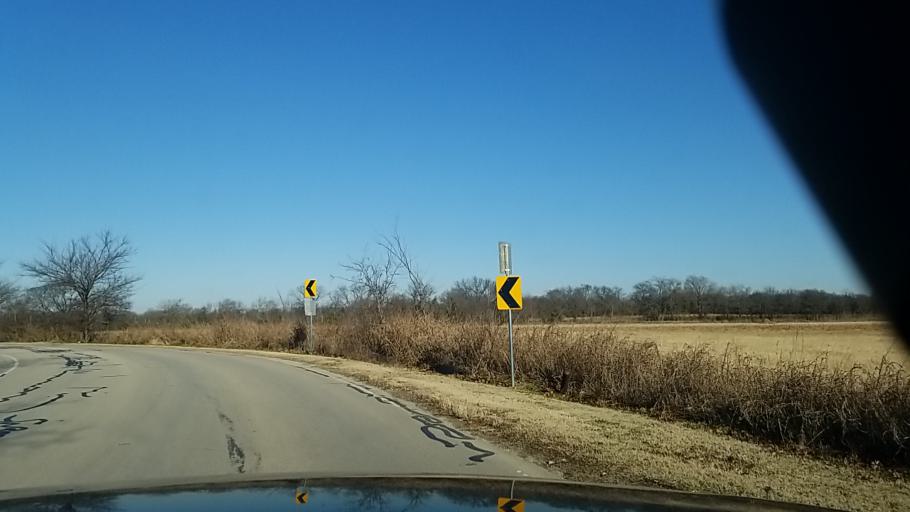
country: US
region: Texas
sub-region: Denton County
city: Argyle
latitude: 33.1480
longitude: -97.1356
